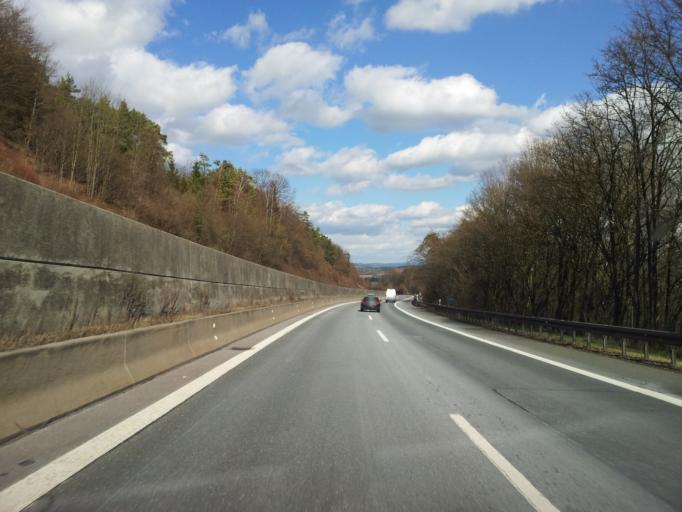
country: DE
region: Bavaria
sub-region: Upper Franconia
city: Kasendorf
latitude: 50.0115
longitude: 11.3669
